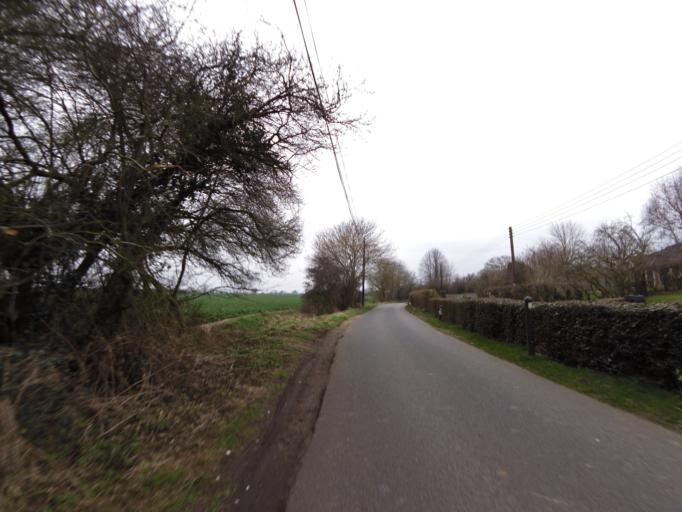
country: GB
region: England
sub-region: Suffolk
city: Framlingham
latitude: 52.2204
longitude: 1.3342
